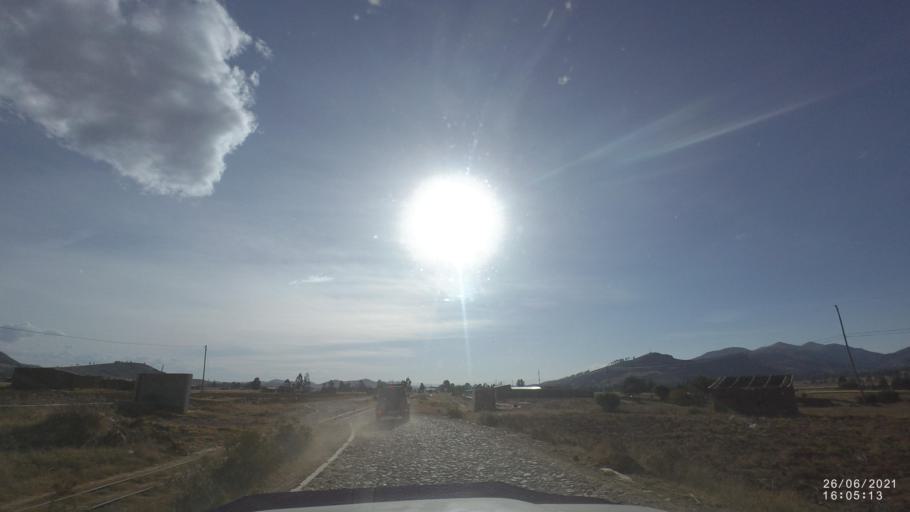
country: BO
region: Cochabamba
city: Arani
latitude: -17.8294
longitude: -65.7608
